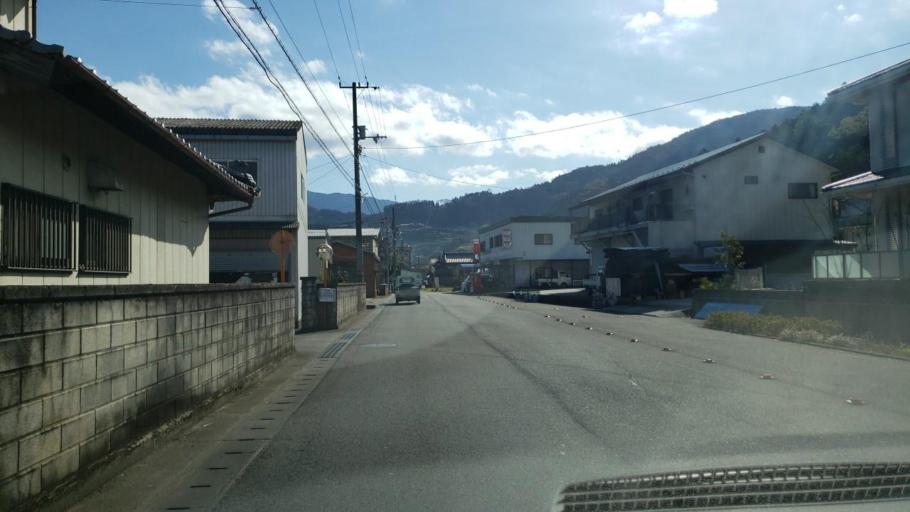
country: JP
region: Tokushima
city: Wakimachi
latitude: 34.0336
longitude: 134.0291
